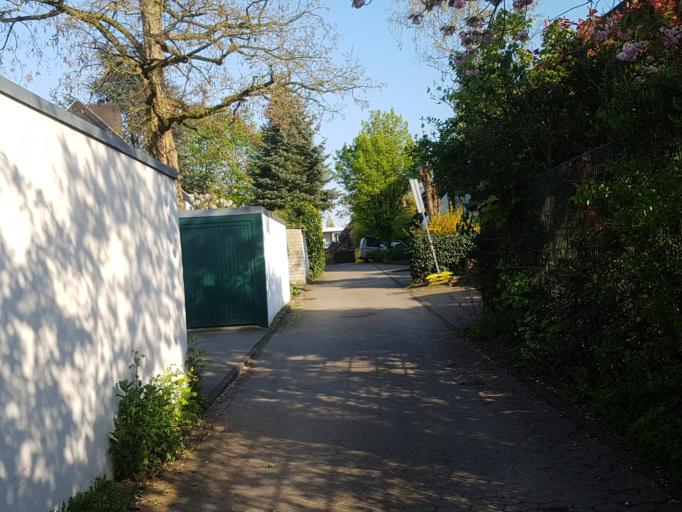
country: DE
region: North Rhine-Westphalia
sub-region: Regierungsbezirk Dusseldorf
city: Meerbusch
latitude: 51.3322
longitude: 6.7225
